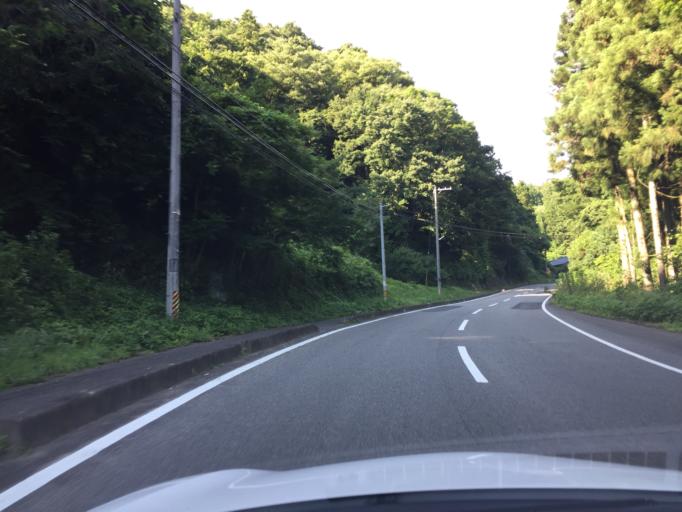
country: JP
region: Fukushima
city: Sukagawa
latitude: 37.3131
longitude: 140.4850
